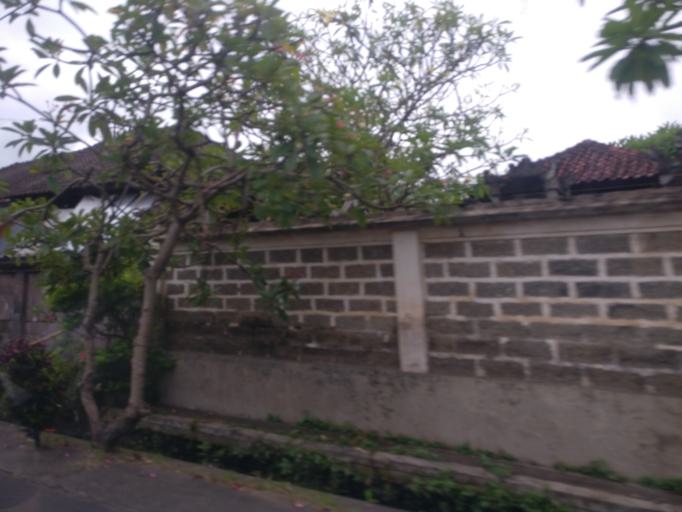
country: ID
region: Bali
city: Banjar Desa
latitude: -8.5712
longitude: 115.2969
